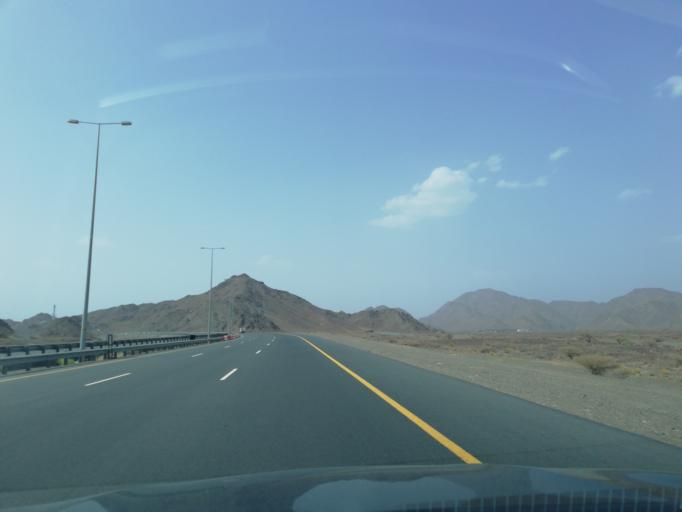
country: OM
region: Ash Sharqiyah
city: Ibra'
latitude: 22.9583
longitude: 58.2455
